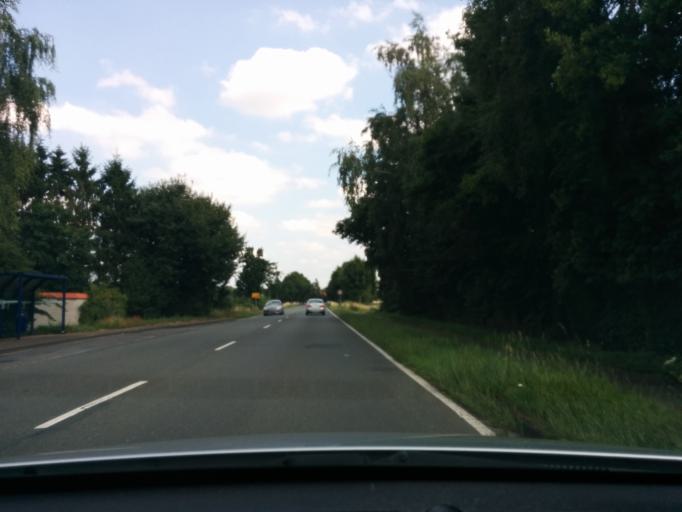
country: DE
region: North Rhine-Westphalia
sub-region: Regierungsbezirk Munster
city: Ochtrup
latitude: 52.1967
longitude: 7.2404
